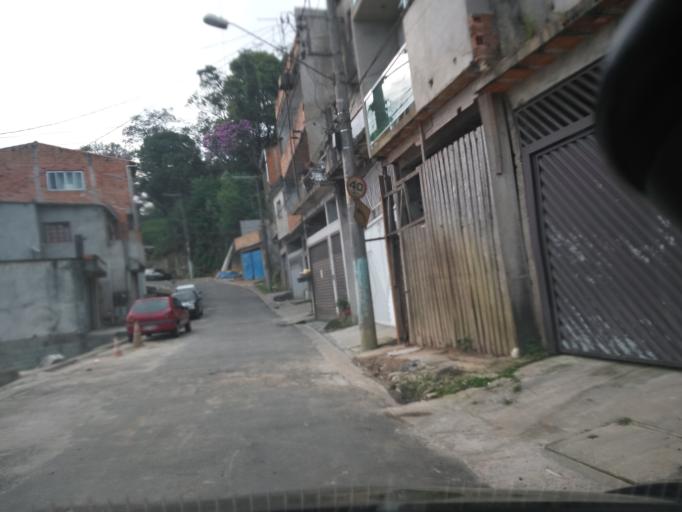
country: BR
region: Sao Paulo
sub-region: Sao Bernardo Do Campo
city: Sao Bernardo do Campo
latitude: -23.8001
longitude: -46.5347
